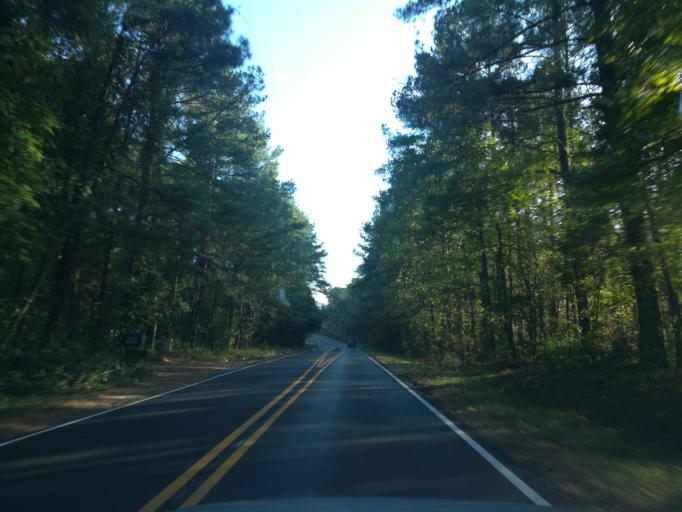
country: US
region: North Carolina
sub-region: Orange County
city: Chapel Hill
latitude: 35.9657
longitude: -79.0346
